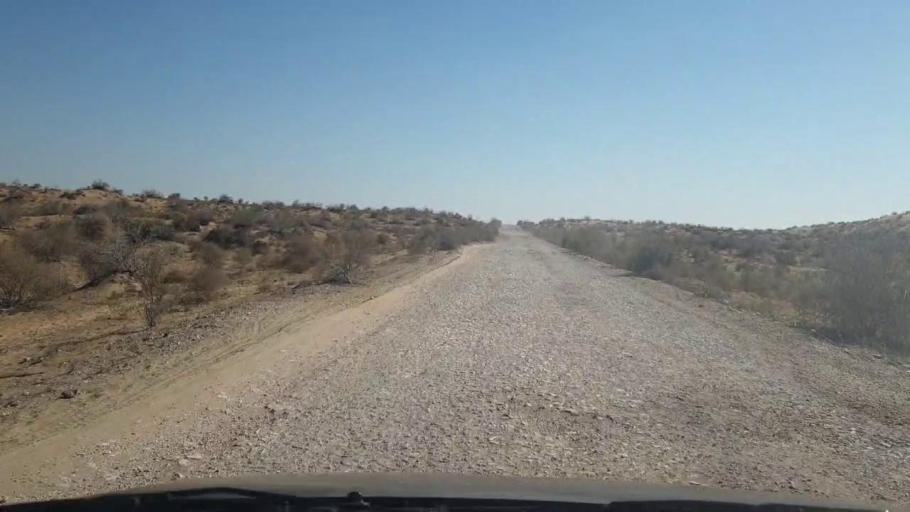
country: PK
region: Sindh
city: Bozdar
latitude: 27.0275
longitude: 68.7089
